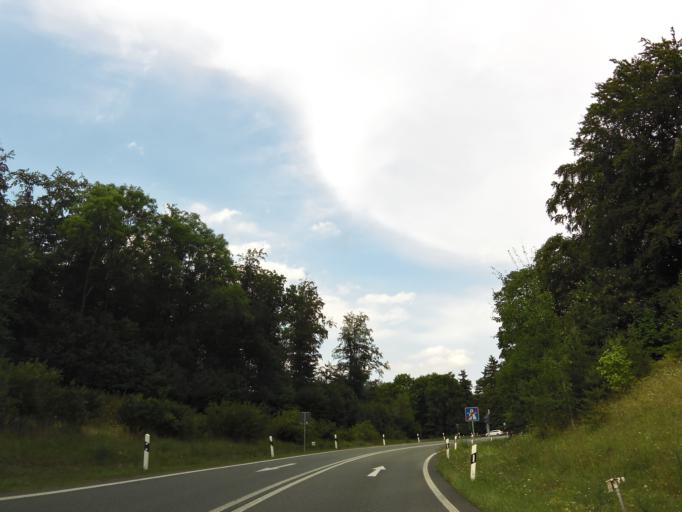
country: DE
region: Thuringia
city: Klettbach
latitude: 50.9268
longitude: 11.1364
